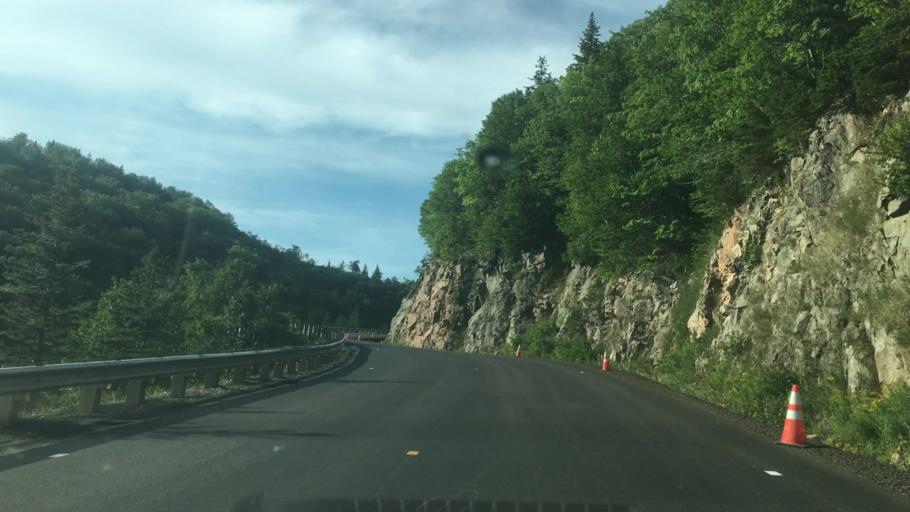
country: CA
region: Nova Scotia
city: Sydney Mines
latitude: 46.8179
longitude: -60.6515
